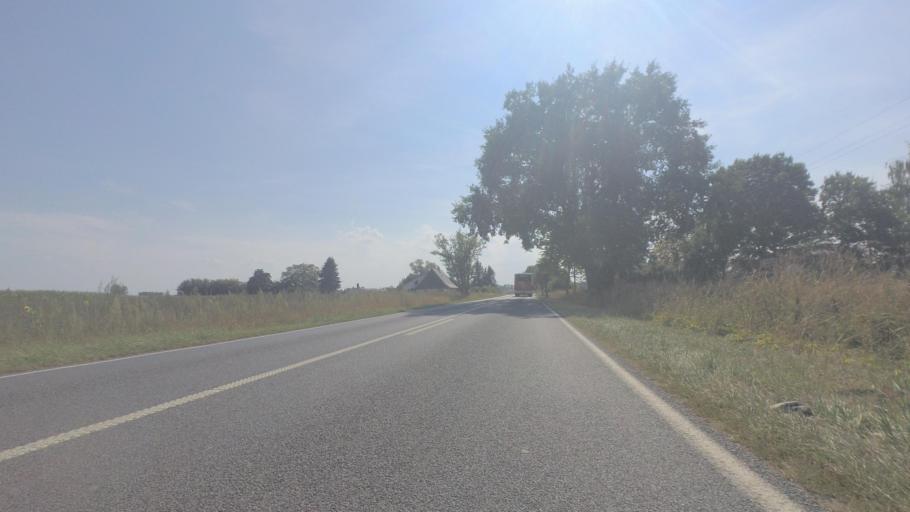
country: DE
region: Mecklenburg-Vorpommern
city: Brandshagen
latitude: 54.1617
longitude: 13.1691
